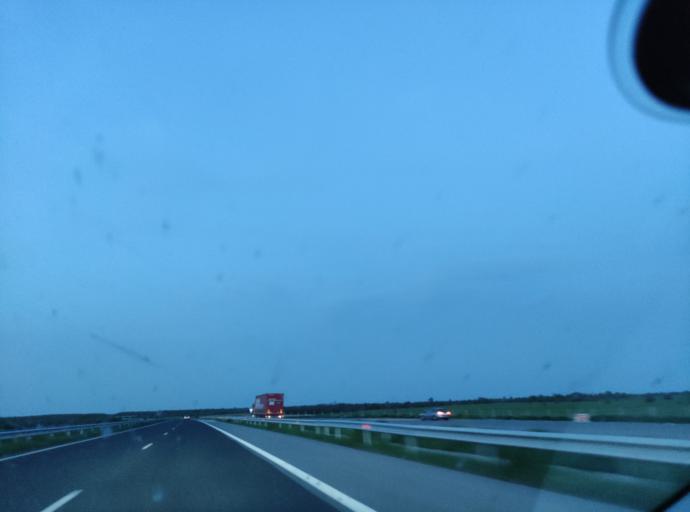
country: BG
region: Stara Zagora
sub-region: Obshtina Stara Zagora
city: Stara Zagora
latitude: 42.3471
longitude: 25.7204
